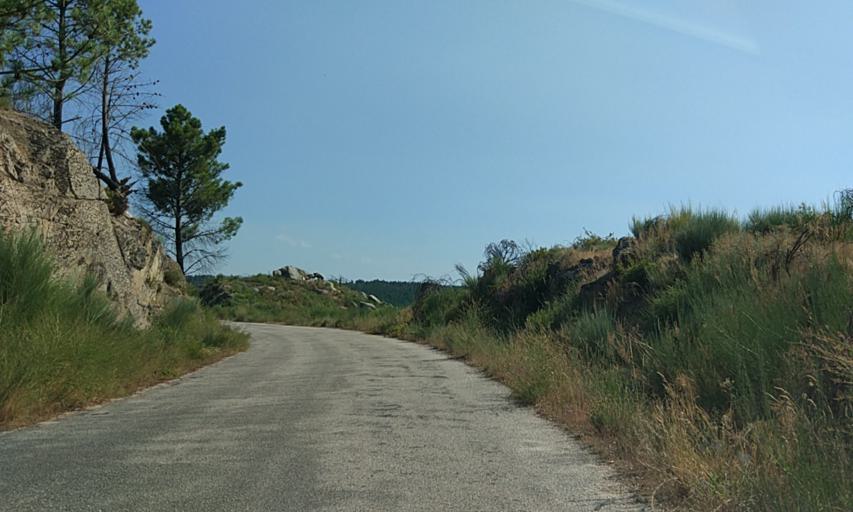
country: PT
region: Vila Real
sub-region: Sabrosa
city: Sabrosa
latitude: 41.3049
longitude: -7.4861
